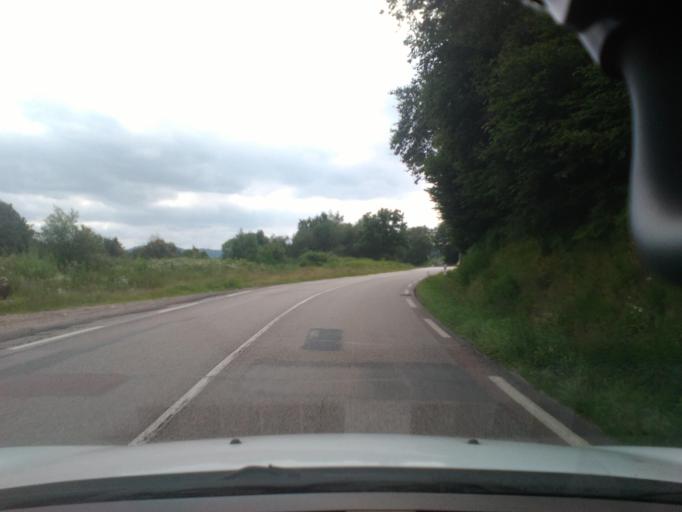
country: FR
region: Lorraine
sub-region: Departement des Vosges
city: Bruyeres
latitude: 48.1926
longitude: 6.6935
